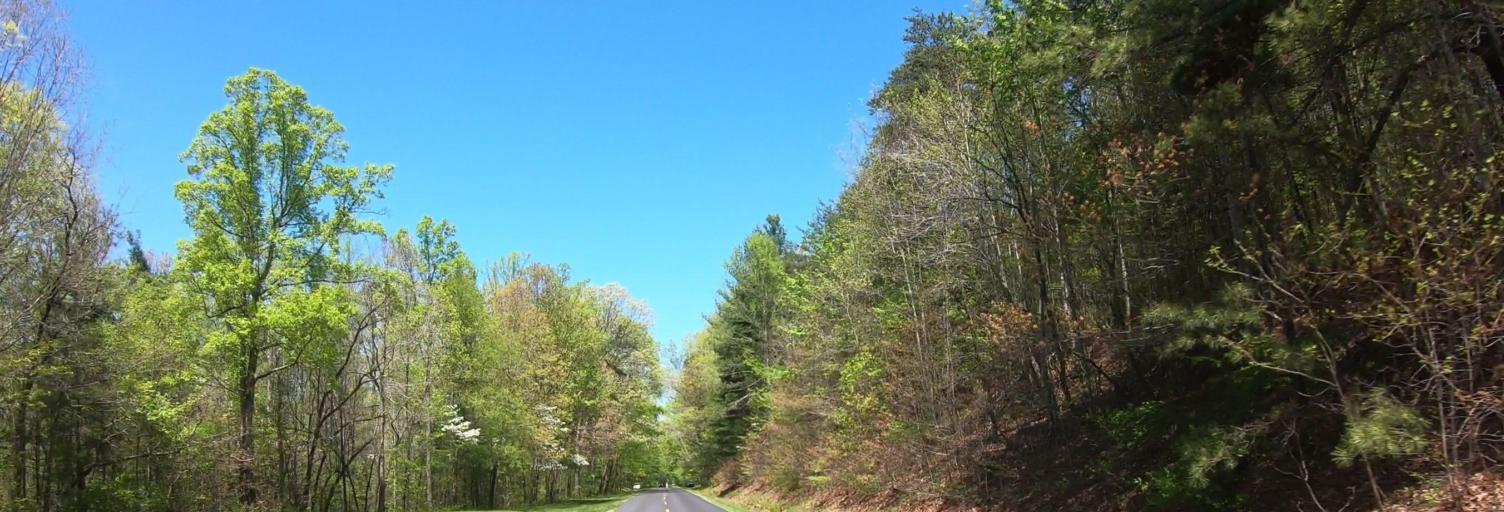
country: US
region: North Carolina
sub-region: Buncombe County
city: Biltmore Forest
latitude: 35.5553
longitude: -82.4961
